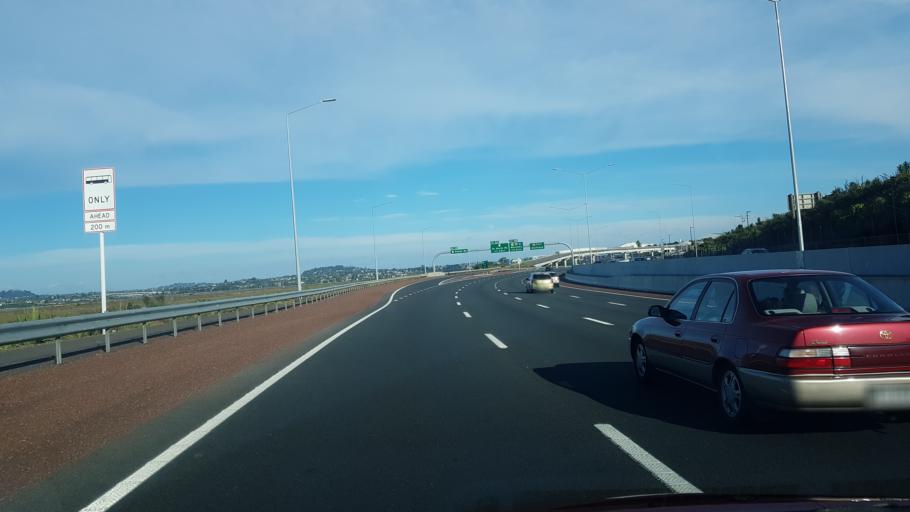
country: NZ
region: Auckland
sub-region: Auckland
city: Rosebank
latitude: -36.8614
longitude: 174.6629
